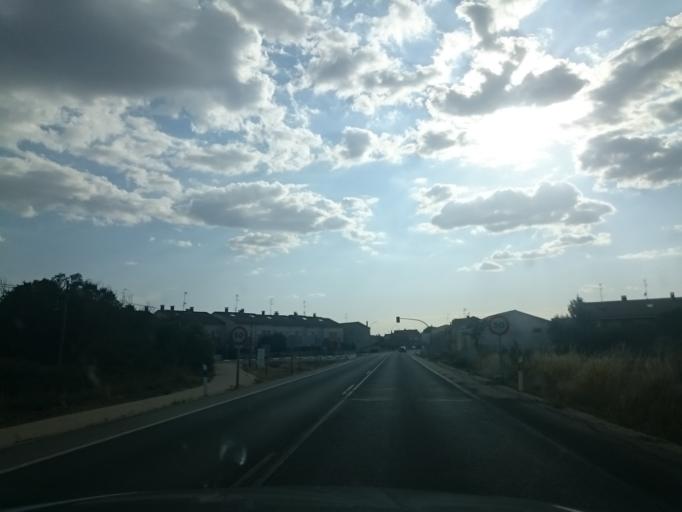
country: ES
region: Castille and Leon
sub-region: Provincia de Burgos
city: Ibeas de Juarros
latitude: 42.3319
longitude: -3.5307
